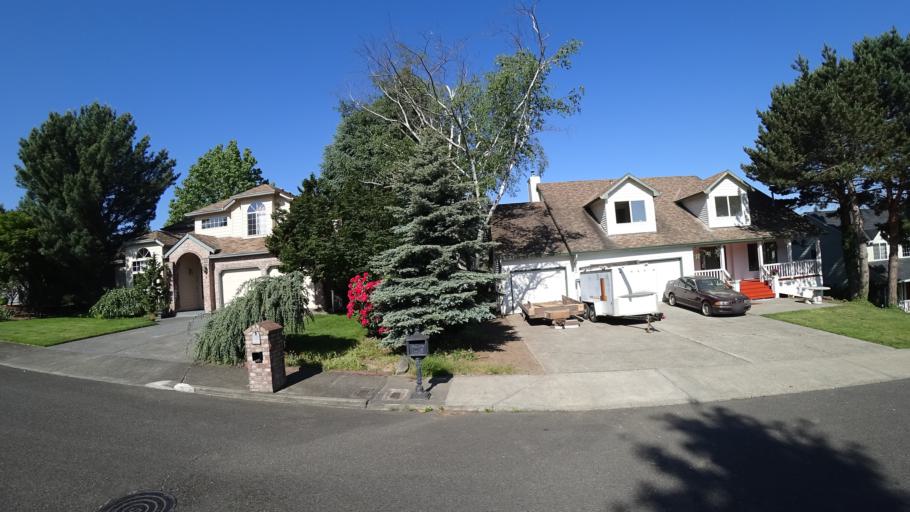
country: US
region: Oregon
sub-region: Multnomah County
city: Lents
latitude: 45.4676
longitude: -122.5505
